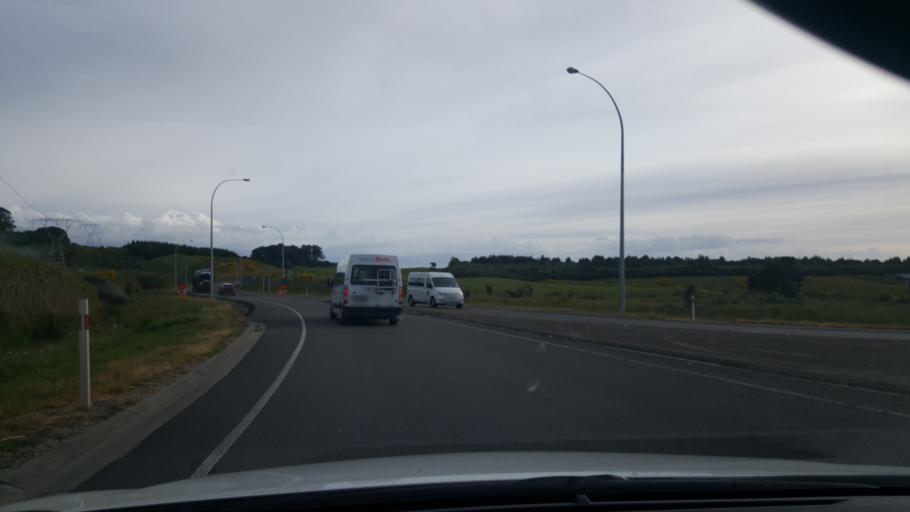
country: NZ
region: Waikato
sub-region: Taupo District
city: Taupo
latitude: -38.7046
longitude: 176.1123
